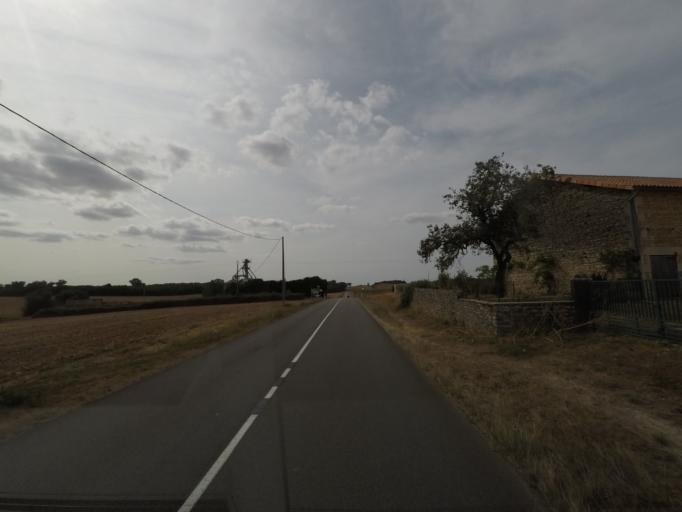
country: FR
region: Poitou-Charentes
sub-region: Departement de la Charente
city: Nanteuil-en-Vallee
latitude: 46.0186
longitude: 0.2746
